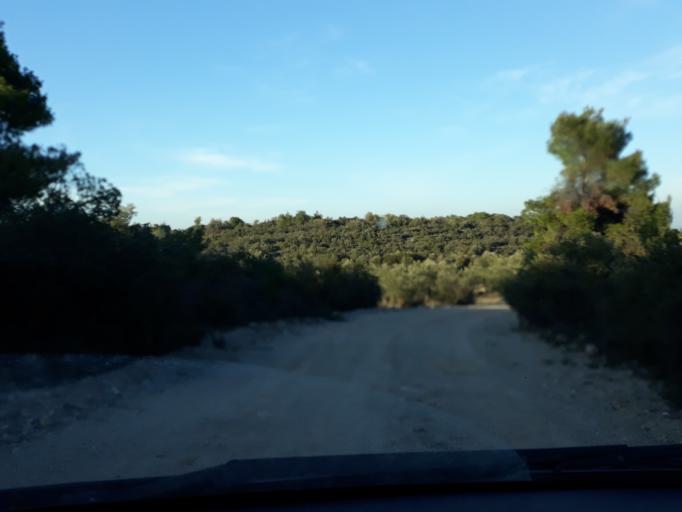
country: GR
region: Central Greece
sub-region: Nomos Voiotias
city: Asopia
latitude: 38.2536
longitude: 23.5312
